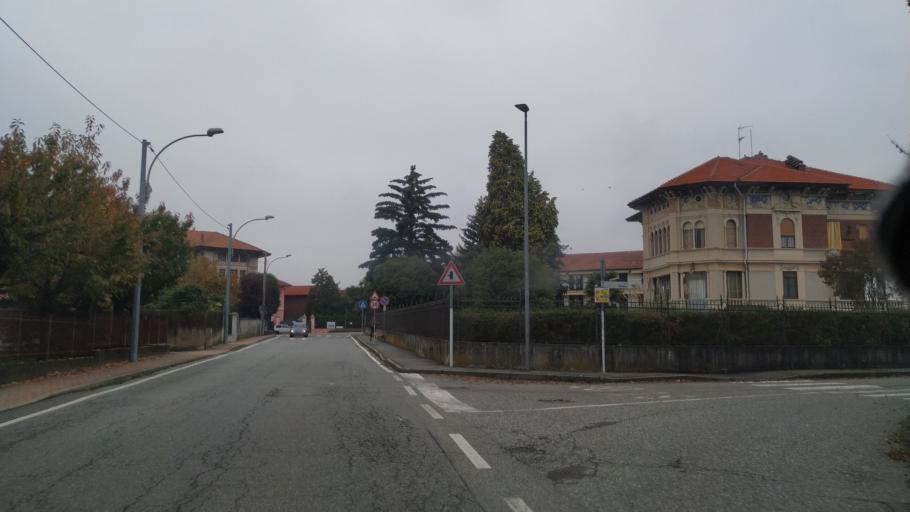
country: IT
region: Piedmont
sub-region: Provincia di Biella
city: Lessona
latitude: 45.5872
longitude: 8.1938
